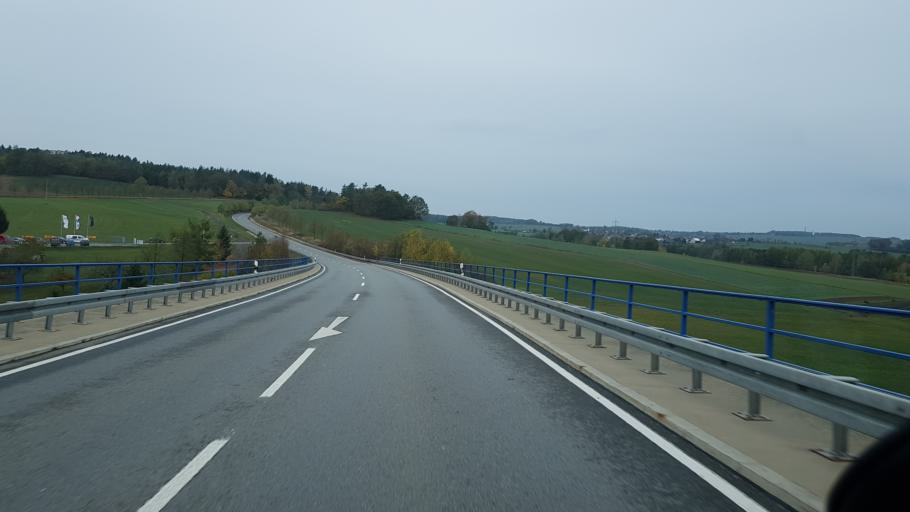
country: DE
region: Saxony
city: Hirschfeld
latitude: 50.6168
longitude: 12.4853
